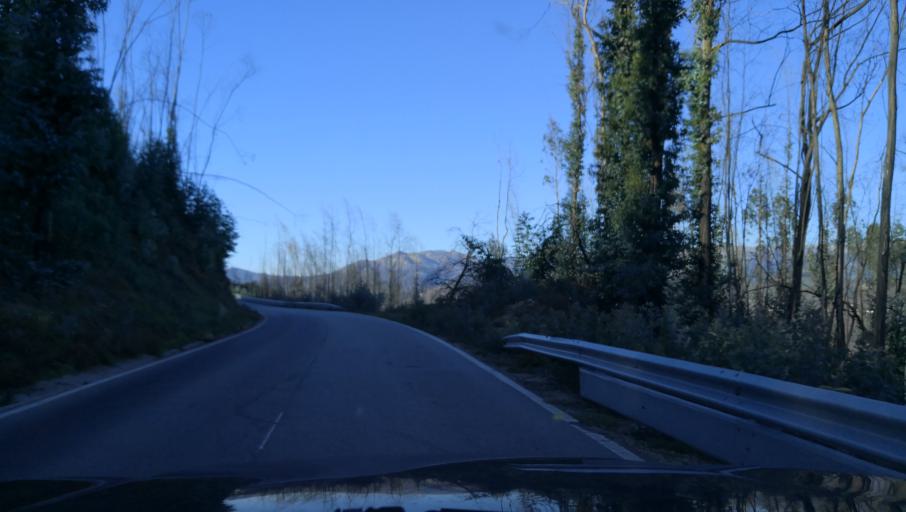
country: PT
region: Viseu
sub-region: Vouzela
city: Vouzela
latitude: 40.7284
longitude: -8.1356
